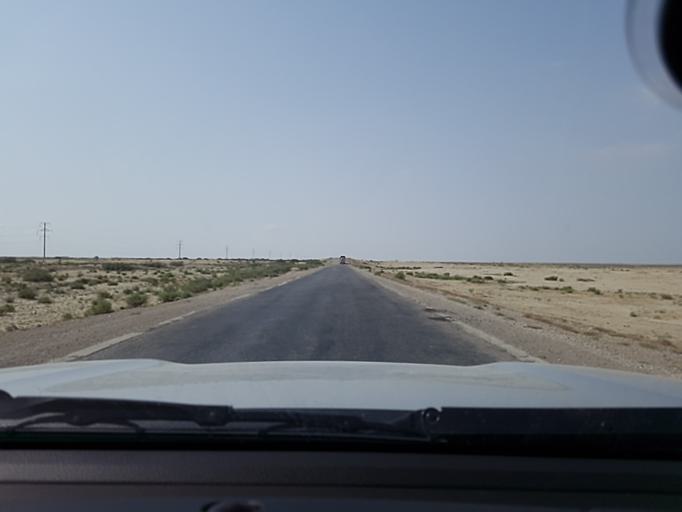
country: TM
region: Balkan
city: Gumdag
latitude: 38.9680
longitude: 54.5882
